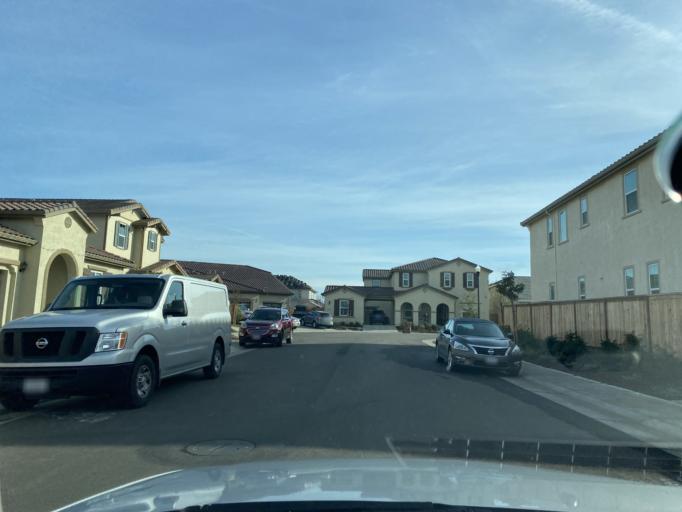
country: US
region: California
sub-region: Sacramento County
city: Elk Grove
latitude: 38.3939
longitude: -121.3863
